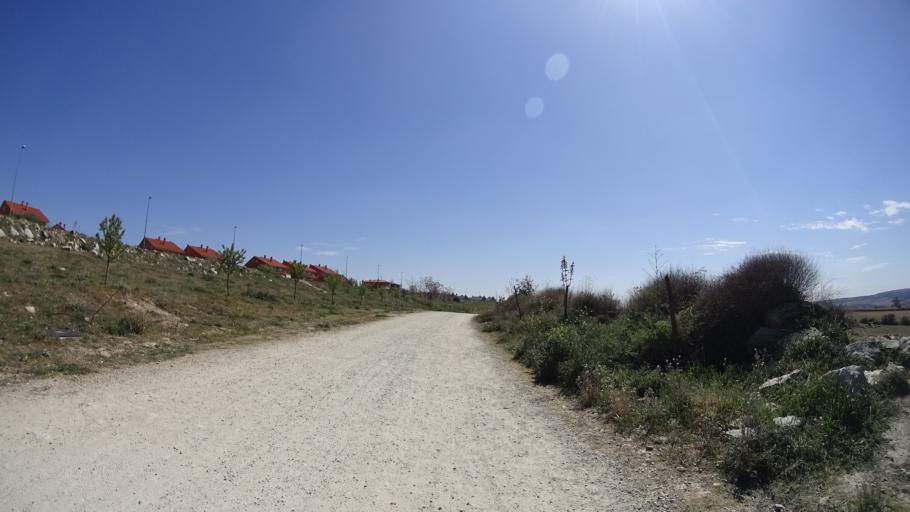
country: ES
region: Madrid
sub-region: Provincia de Madrid
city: Colmenar Viejo
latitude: 40.6690
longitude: -3.7854
